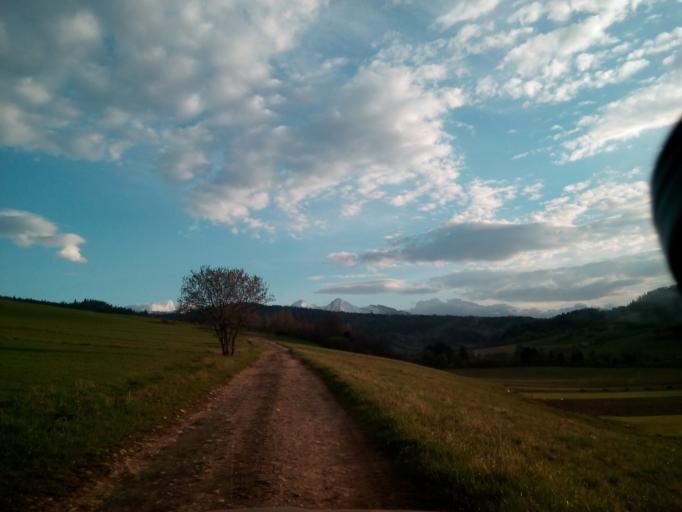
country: PL
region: Lesser Poland Voivodeship
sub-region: Powiat nowotarski
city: Niedzica
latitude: 49.3487
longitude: 20.2895
